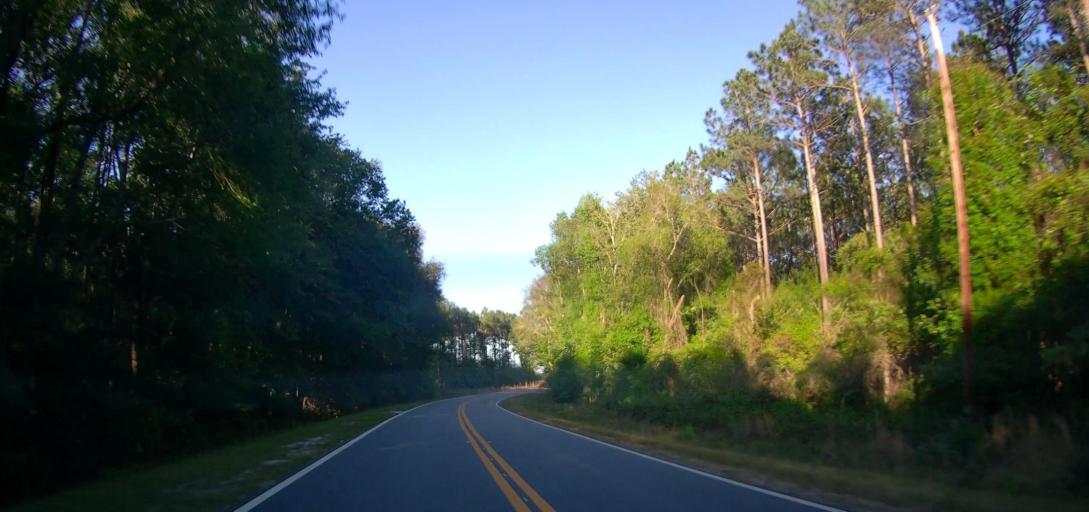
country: US
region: Georgia
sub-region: Ben Hill County
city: Fitzgerald
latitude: 31.6579
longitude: -83.1588
